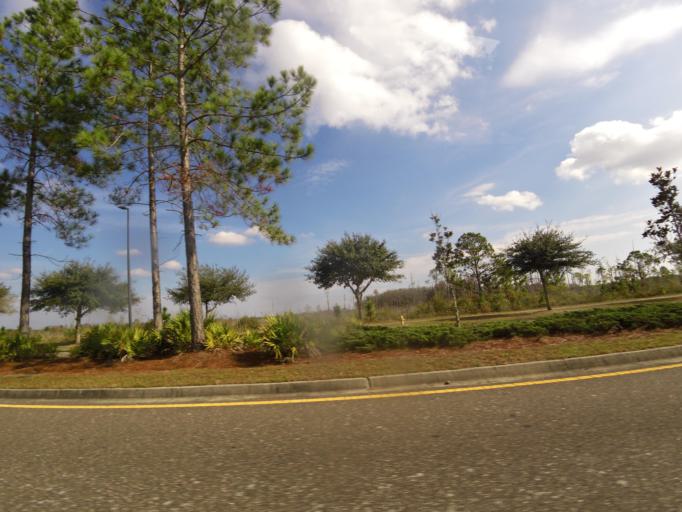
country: US
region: Florida
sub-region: Duval County
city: Baldwin
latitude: 30.2658
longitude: -81.8867
